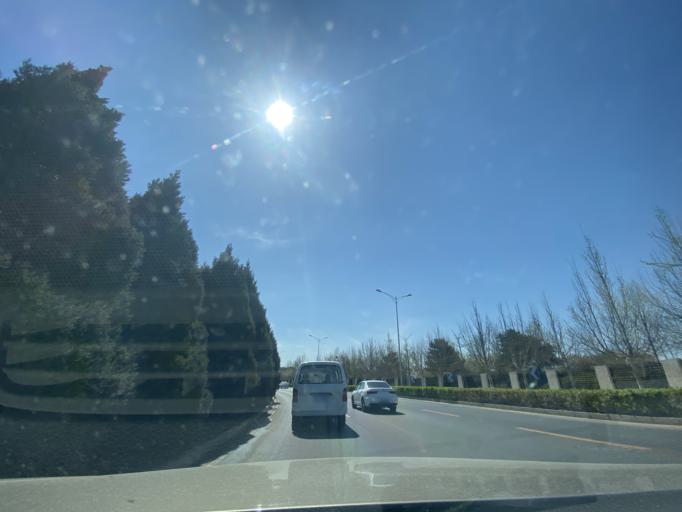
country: CN
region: Beijing
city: Sijiqing
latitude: 39.9382
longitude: 116.2404
